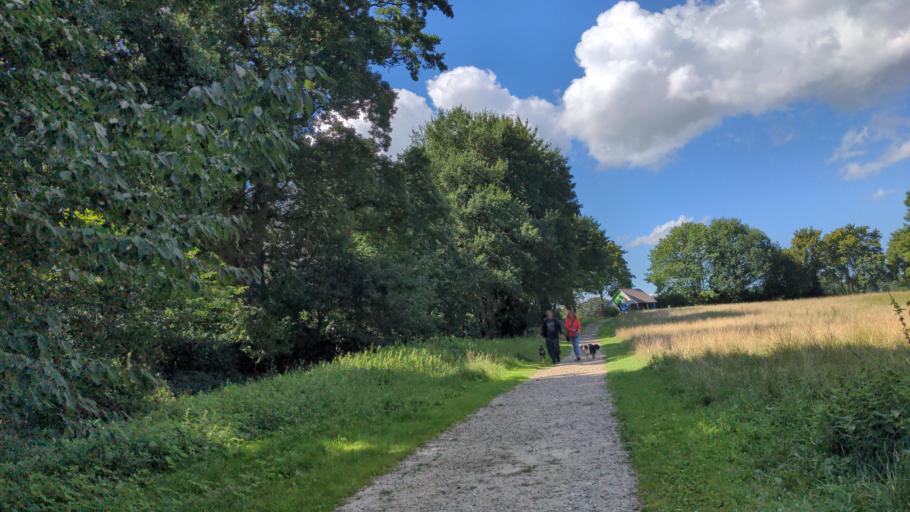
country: DE
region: Schleswig-Holstein
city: Lensahn
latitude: 54.2100
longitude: 10.8725
